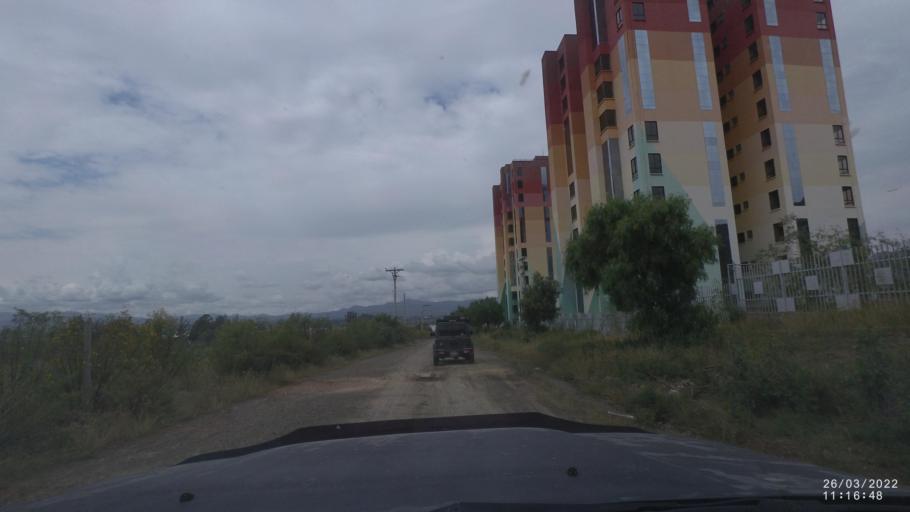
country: BO
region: Cochabamba
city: Tarata
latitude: -17.5366
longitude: -66.0233
